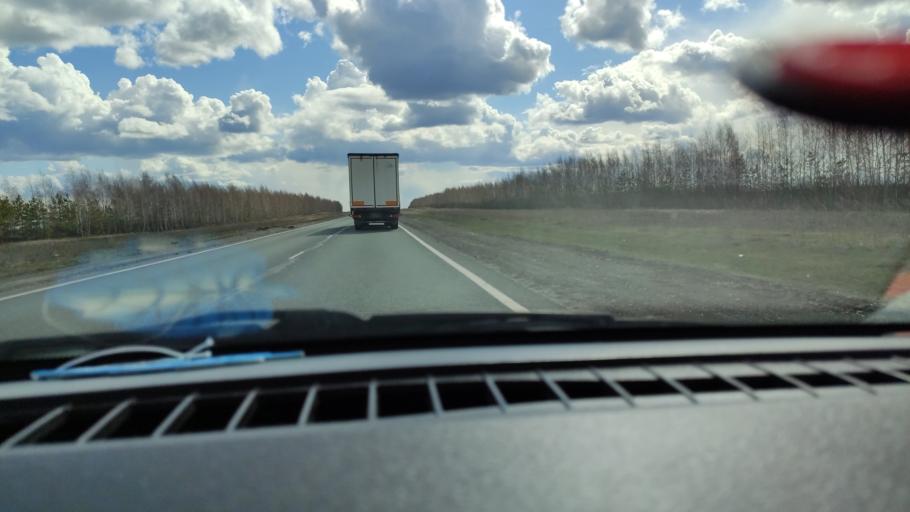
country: RU
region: Saratov
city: Dukhovnitskoye
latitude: 52.8157
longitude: 48.2315
